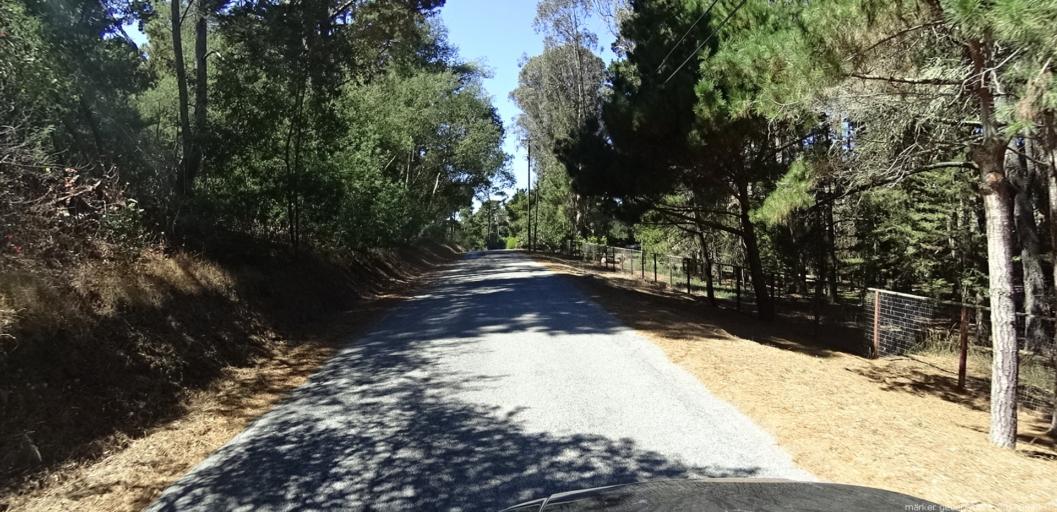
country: US
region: California
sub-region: Monterey County
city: Carmel-by-the-Sea
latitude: 36.5677
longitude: -121.8935
